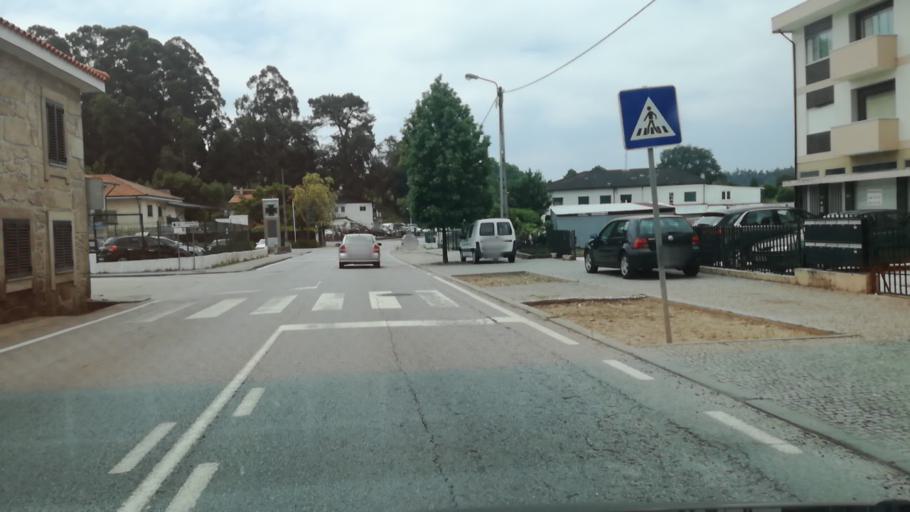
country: PT
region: Porto
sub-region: Trofa
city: Sao Romao do Coronado
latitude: 41.2991
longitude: -8.5964
